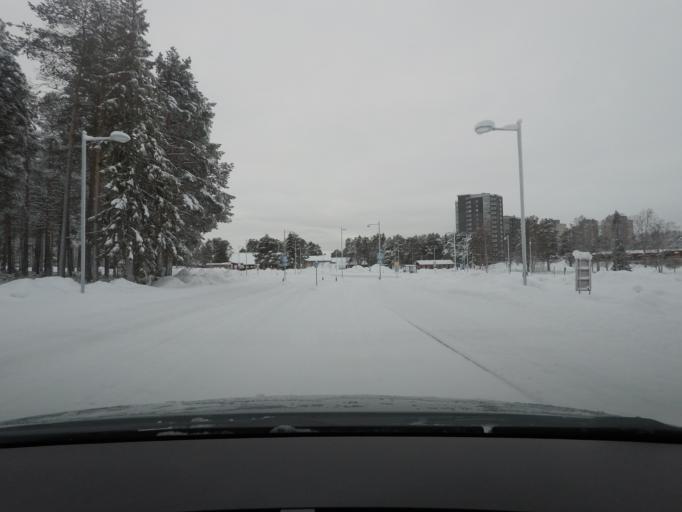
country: SE
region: Norrbotten
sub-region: Lulea Kommun
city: Lulea
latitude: 65.5938
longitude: 22.1896
